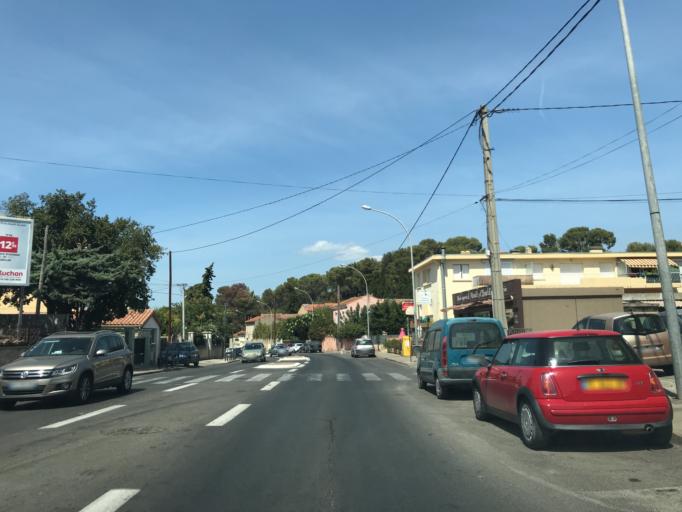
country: FR
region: Provence-Alpes-Cote d'Azur
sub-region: Departement du Var
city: La Seyne-sur-Mer
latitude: 43.0905
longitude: 5.8814
